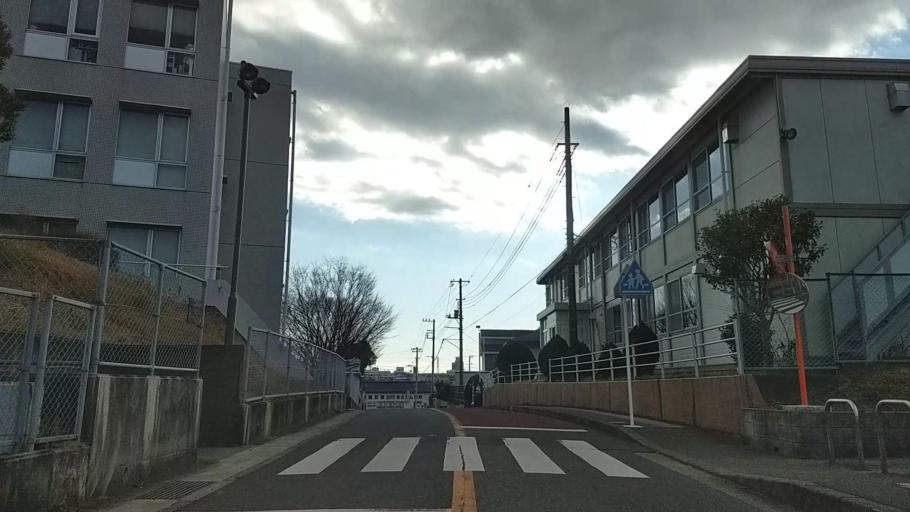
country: JP
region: Kanagawa
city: Isehara
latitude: 35.4070
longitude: 139.3130
